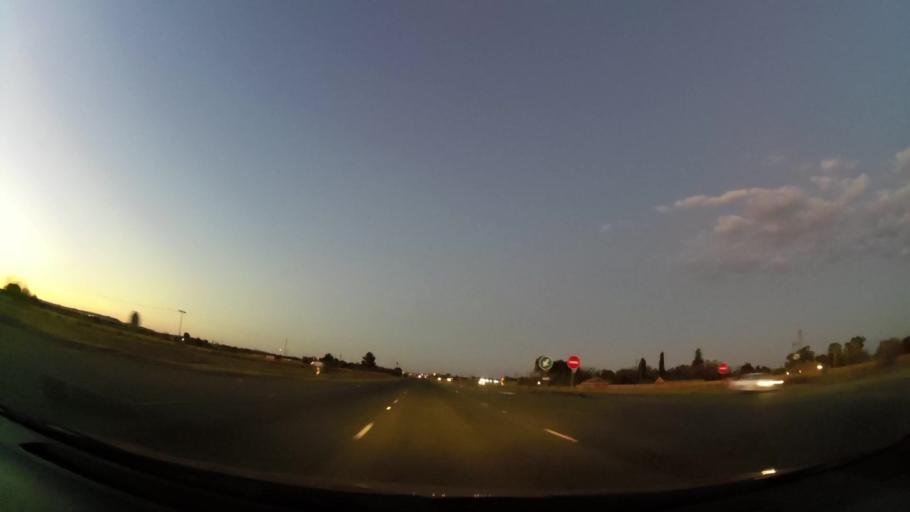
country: ZA
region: North-West
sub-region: Dr Kenneth Kaunda District Municipality
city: Potchefstroom
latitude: -26.7006
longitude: 27.1290
